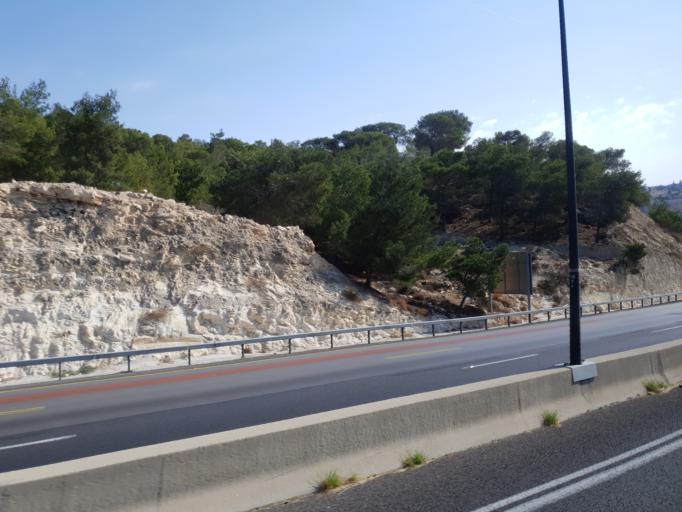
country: PS
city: Az Za`ayyim
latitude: 31.7850
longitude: 35.2811
